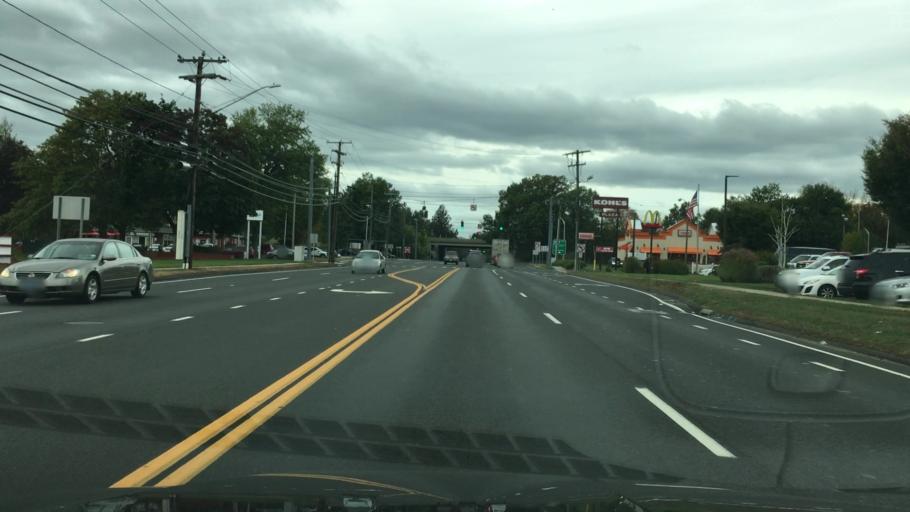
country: US
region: Connecticut
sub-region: Hartford County
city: Thompsonville
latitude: 41.9980
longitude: -72.5827
